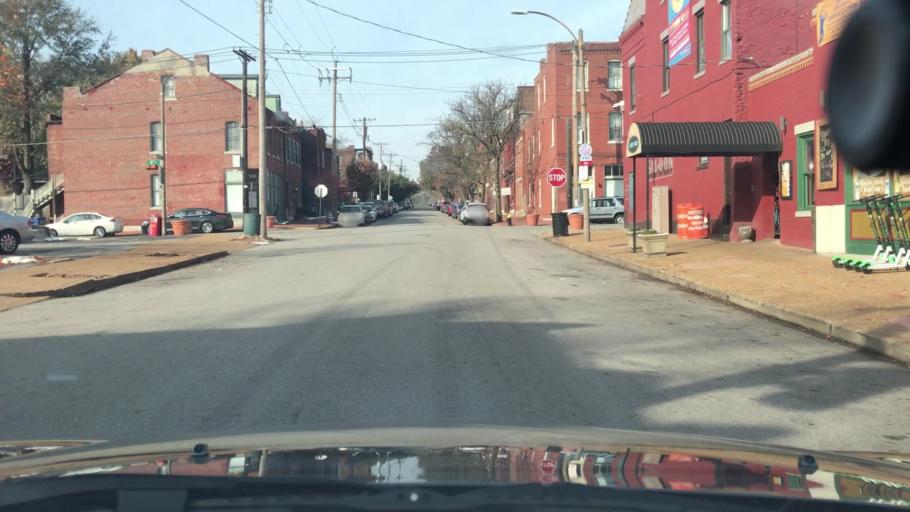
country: US
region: Missouri
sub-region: City of Saint Louis
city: St. Louis
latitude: 38.6083
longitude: -90.2041
